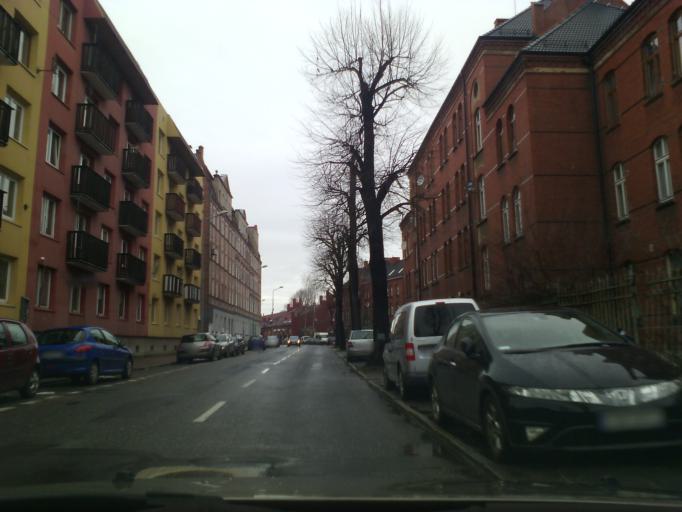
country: PL
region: Lower Silesian Voivodeship
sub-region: Powiat swidnicki
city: Swidnica
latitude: 50.8383
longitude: 16.4753
